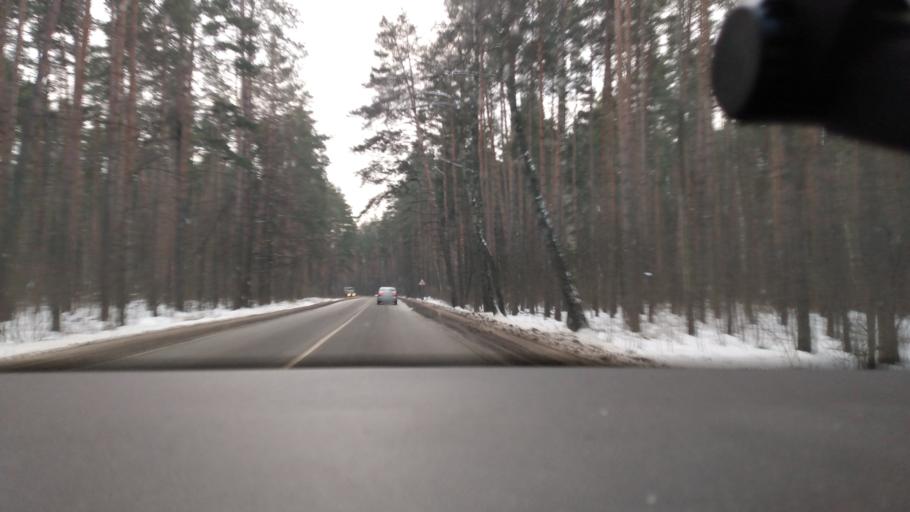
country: RU
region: Moskovskaya
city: Rodniki
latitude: 55.6740
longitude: 38.1055
